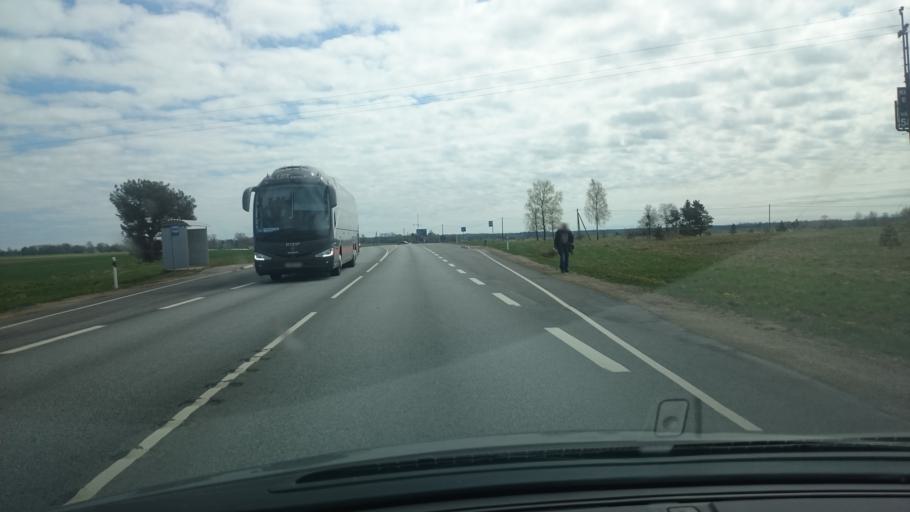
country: EE
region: Ida-Virumaa
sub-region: Puessi linn
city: Pussi
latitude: 59.4039
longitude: 27.0702
